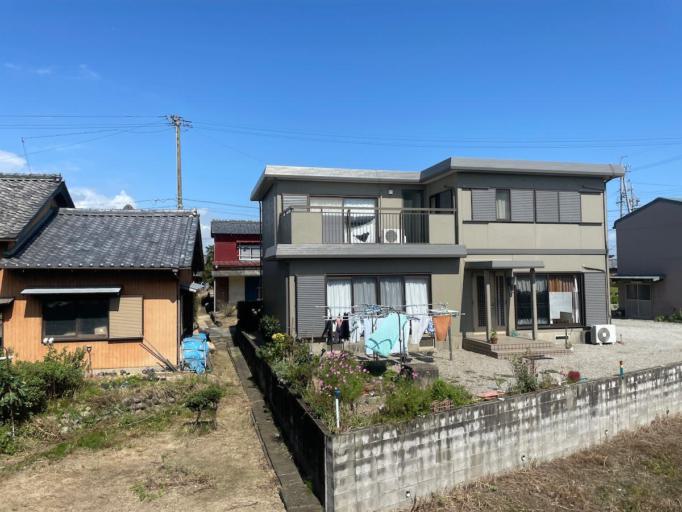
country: JP
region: Mie
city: Suzuka
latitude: 34.8677
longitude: 136.6039
